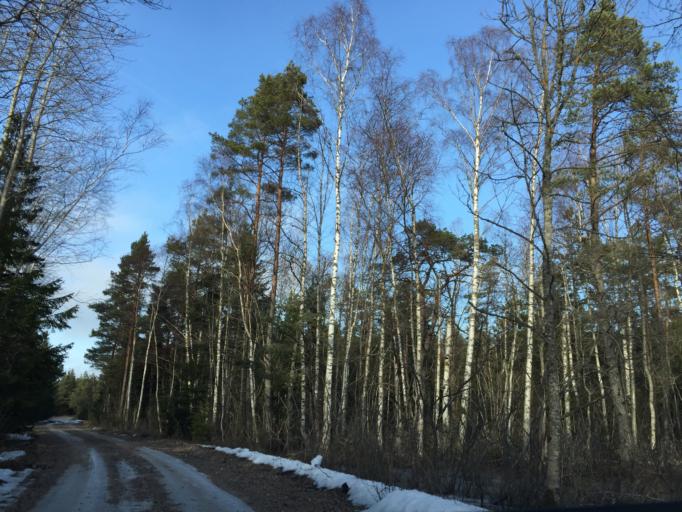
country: EE
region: Saare
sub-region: Kuressaare linn
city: Kuressaare
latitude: 58.4782
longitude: 21.9511
